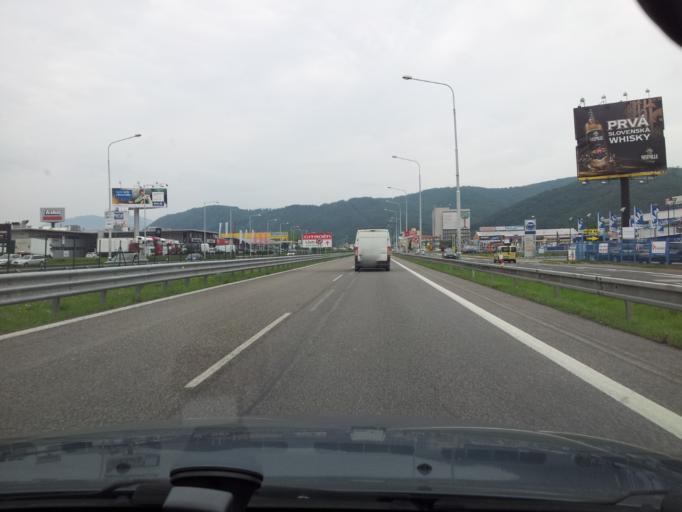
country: SK
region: Banskobystricky
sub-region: Okres Banska Bystrica
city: Banska Bystrica
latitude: 48.7010
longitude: 19.1345
